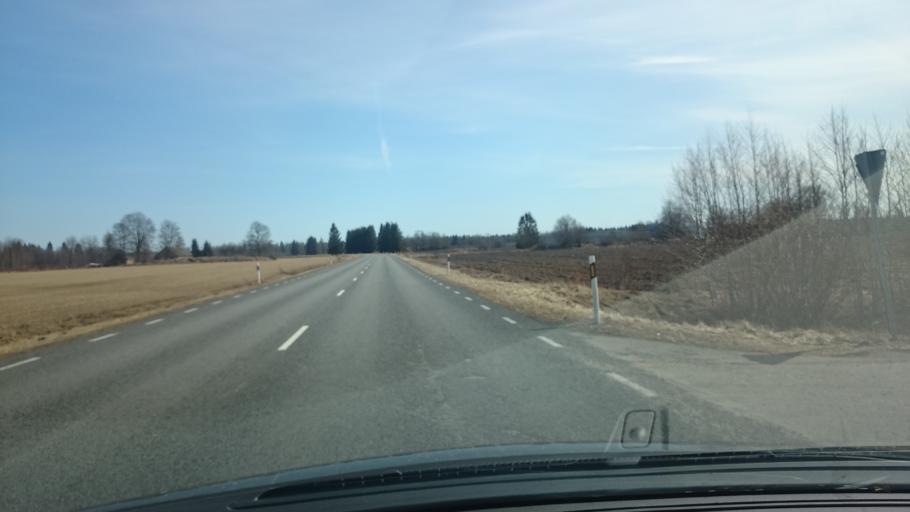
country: EE
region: Paernumaa
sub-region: Tootsi vald
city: Tootsi
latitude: 58.6672
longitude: 24.7797
